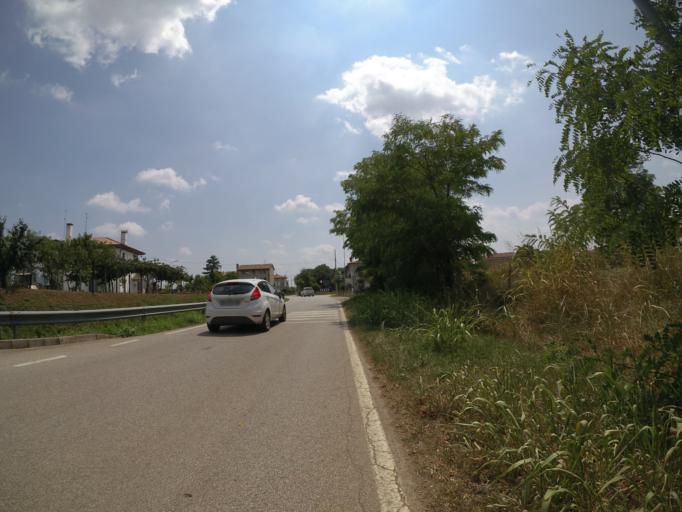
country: IT
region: Friuli Venezia Giulia
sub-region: Provincia di Udine
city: Basiliano
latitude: 45.9816
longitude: 13.0867
